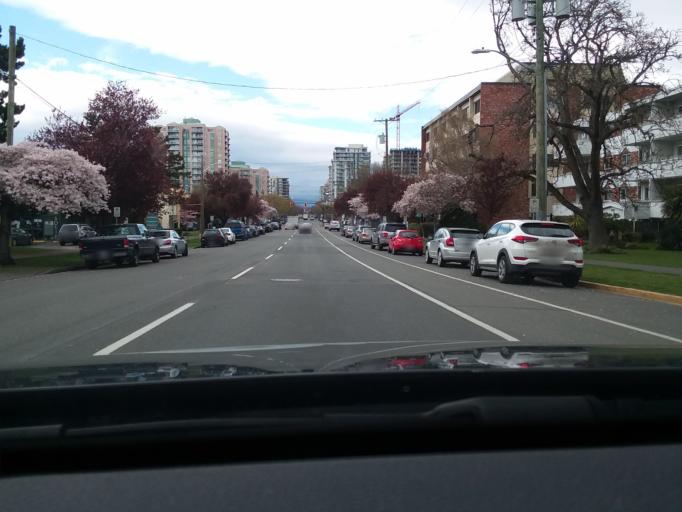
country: CA
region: British Columbia
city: Victoria
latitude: 48.4249
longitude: -123.3514
